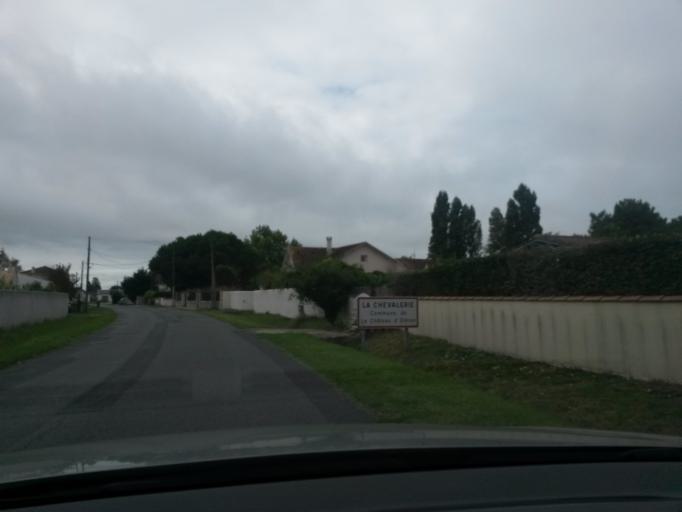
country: FR
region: Poitou-Charentes
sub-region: Departement de la Charente-Maritime
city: Saint-Trojan-les-Bains
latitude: 45.8747
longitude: -1.2132
